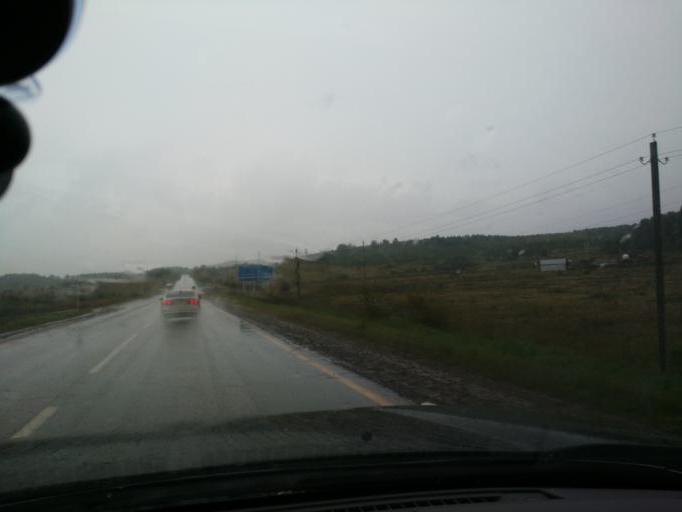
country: RU
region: Perm
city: Osa
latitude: 57.1825
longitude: 55.5853
